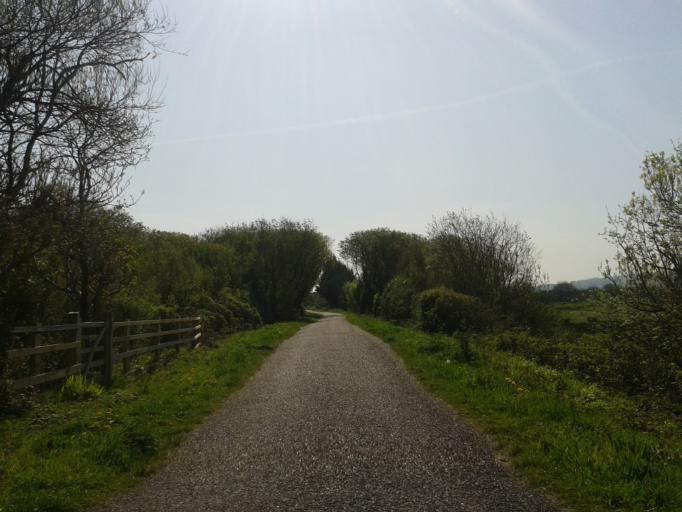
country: GB
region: England
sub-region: Devon
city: Braunton
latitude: 51.0990
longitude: -4.1598
